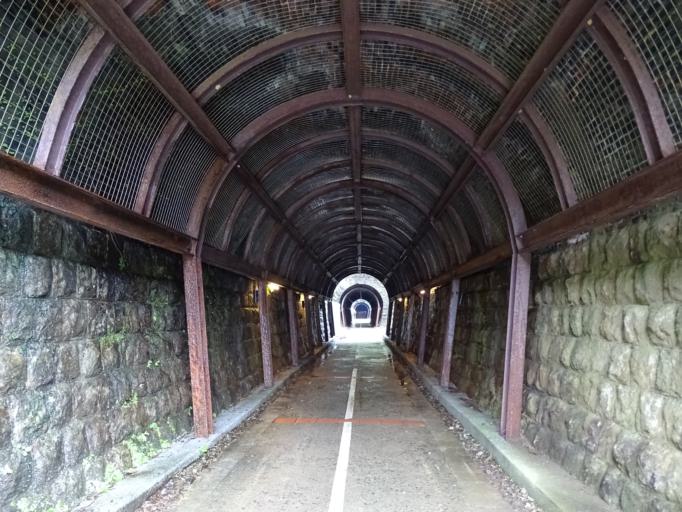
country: TW
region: Taiwan
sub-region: Keelung
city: Keelung
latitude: 25.1024
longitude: 121.8303
